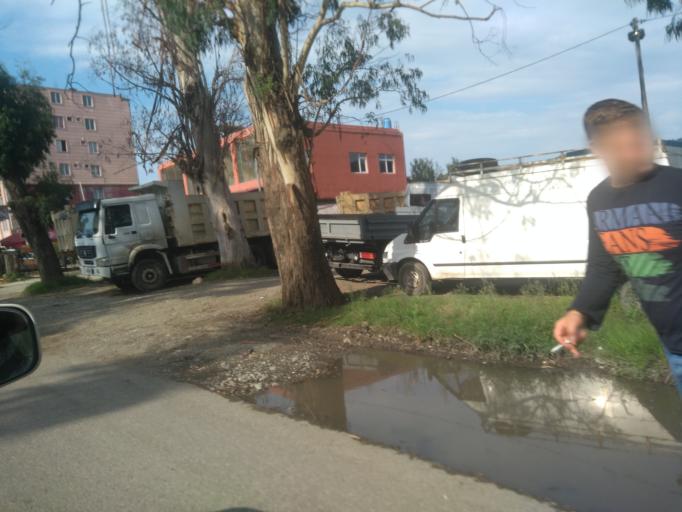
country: GE
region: Ajaria
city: Khelvachauri
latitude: 41.5880
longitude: 41.6491
